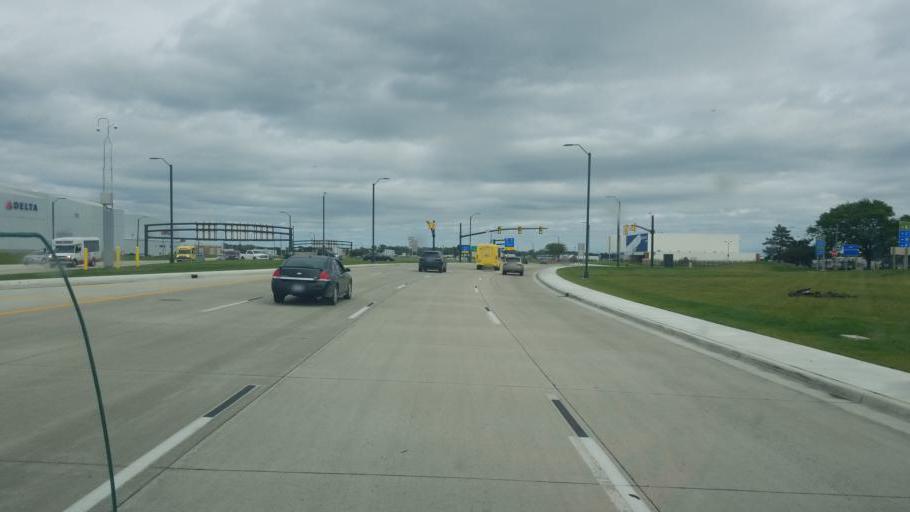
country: US
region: Michigan
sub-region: Wayne County
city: Romulus
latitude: 42.2291
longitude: -83.3433
